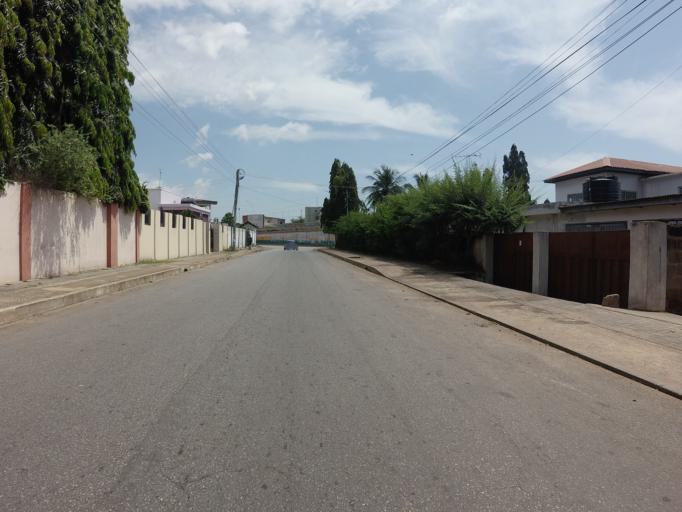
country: GH
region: Greater Accra
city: Accra
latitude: 5.5742
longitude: -0.1992
